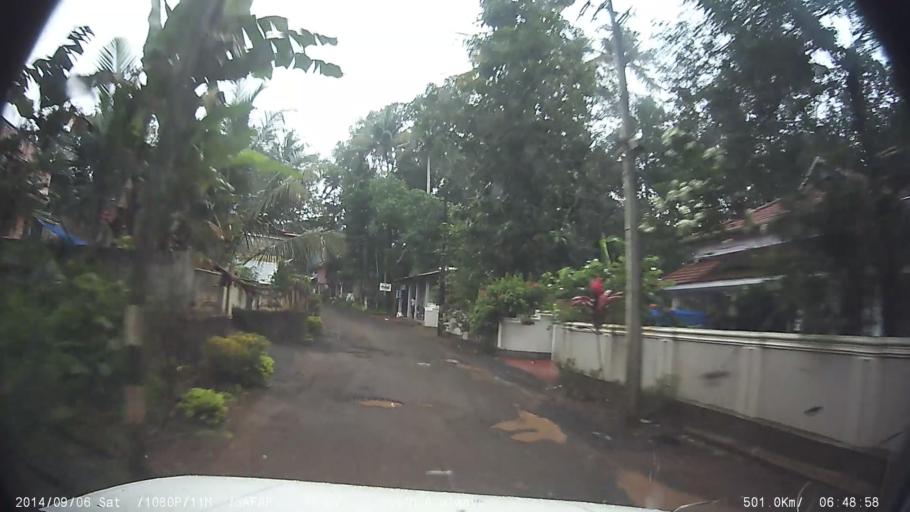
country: IN
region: Kerala
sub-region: Ernakulam
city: Piravam
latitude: 9.7754
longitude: 76.5094
